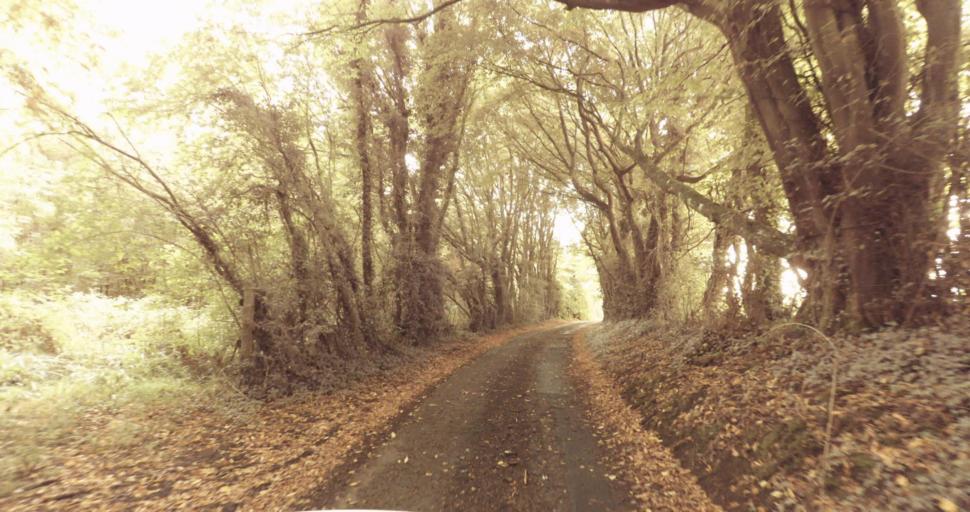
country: FR
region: Lower Normandy
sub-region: Departement de l'Orne
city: Trun
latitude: 48.9153
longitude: 0.0949
